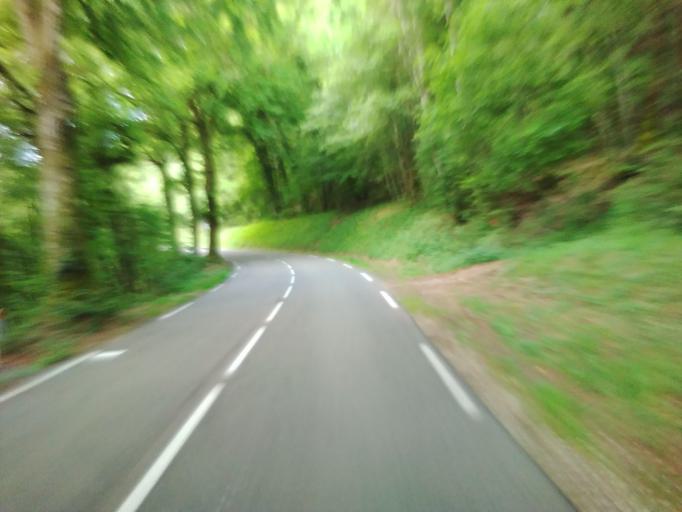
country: FR
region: Franche-Comte
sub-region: Departement du Jura
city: Arbois
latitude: 46.8840
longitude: 5.8001
